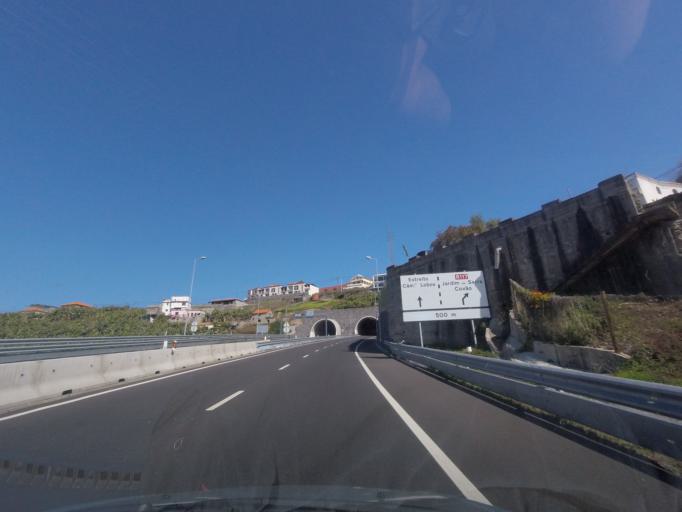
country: PT
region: Madeira
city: Camara de Lobos
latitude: 32.6628
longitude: -16.9683
